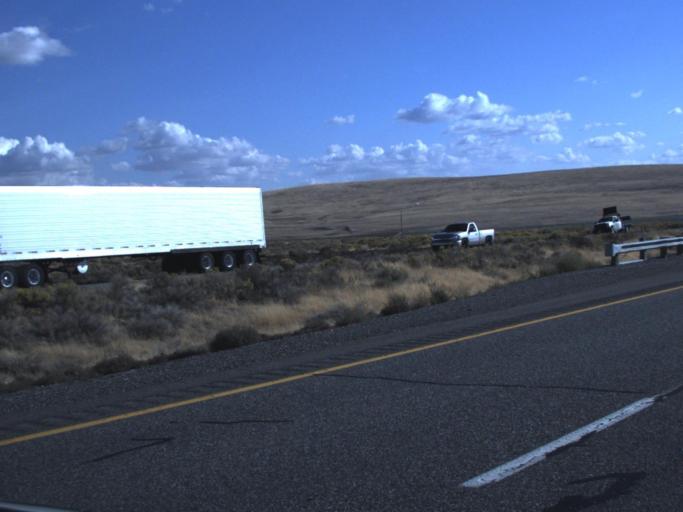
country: US
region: Washington
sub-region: Benton County
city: Highland
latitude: 46.0266
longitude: -119.2250
